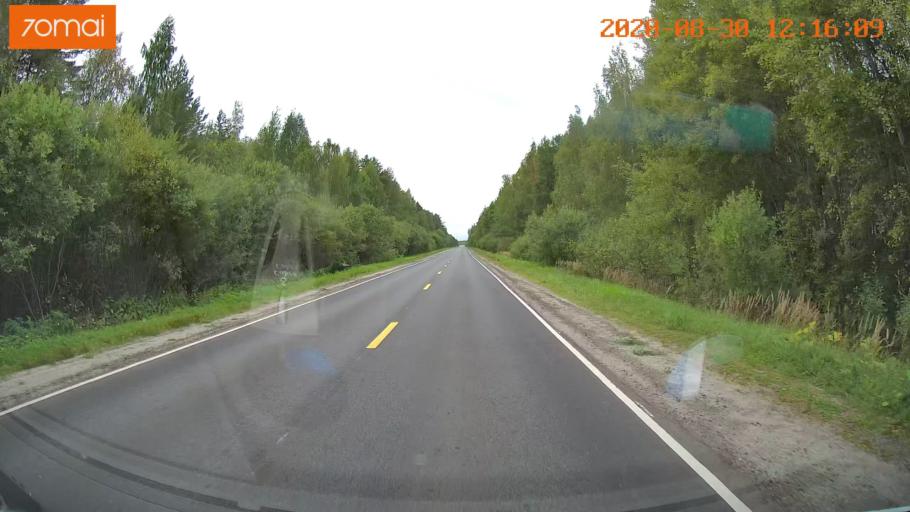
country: RU
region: Ivanovo
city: Yur'yevets
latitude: 57.3196
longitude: 43.0116
